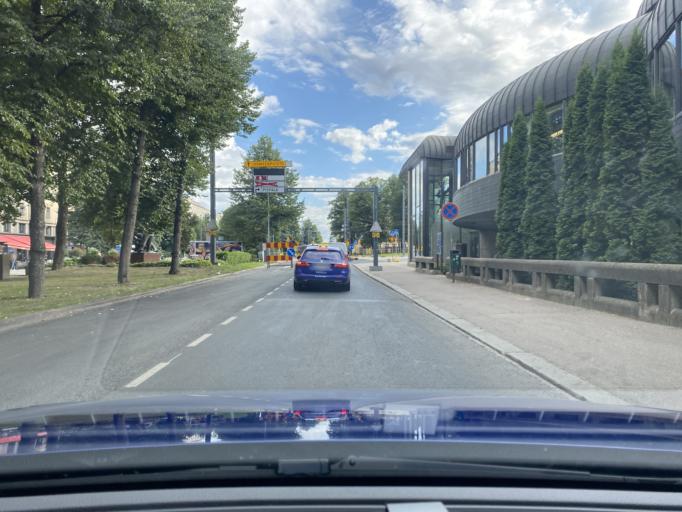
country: FI
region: Pirkanmaa
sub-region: Tampere
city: Tampere
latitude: 61.4984
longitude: 23.7513
